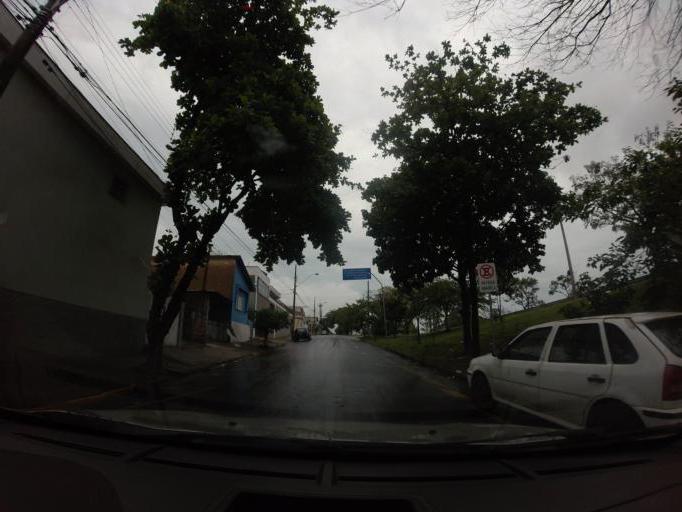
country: BR
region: Sao Paulo
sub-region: Piracicaba
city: Piracicaba
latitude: -22.7394
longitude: -47.6477
